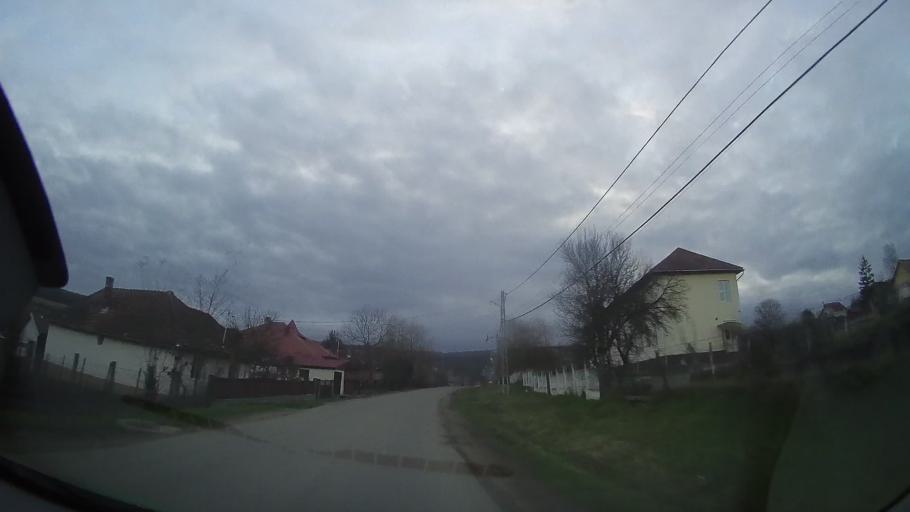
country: RO
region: Cluj
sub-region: Comuna Palatca
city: Palatca
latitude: 46.8410
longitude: 23.9887
